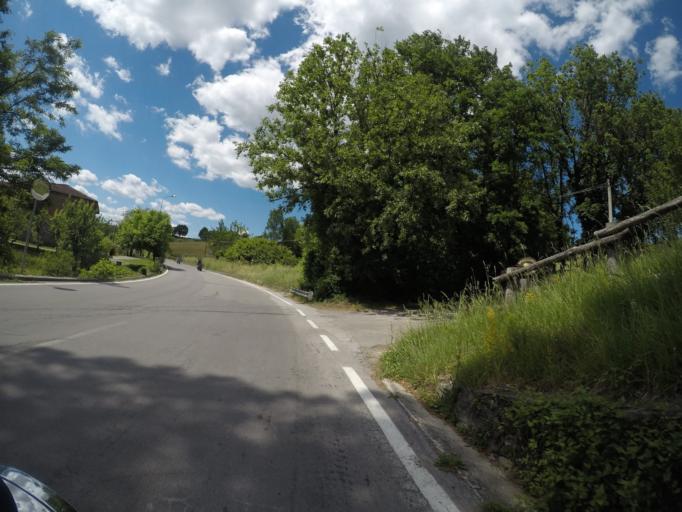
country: IT
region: Tuscany
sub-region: Provincia di Lucca
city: Villa Collemandina
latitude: 44.1417
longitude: 10.3774
